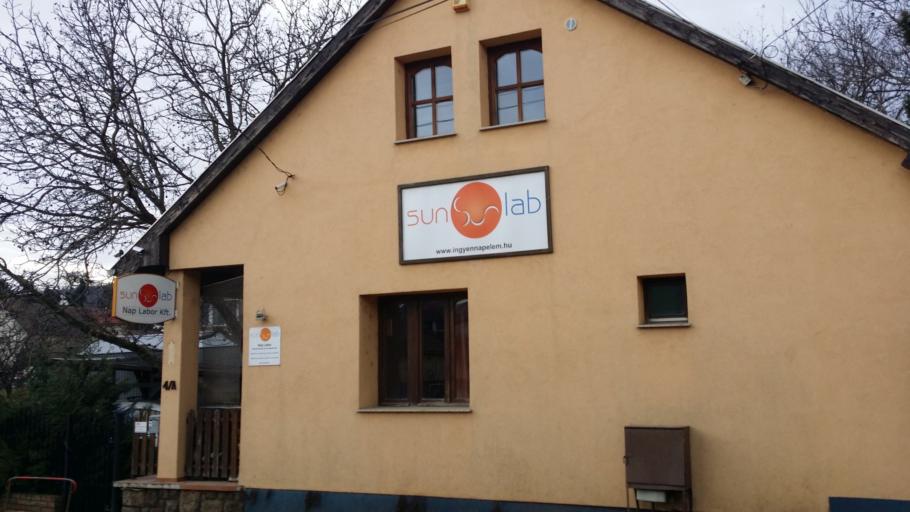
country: HU
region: Pest
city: Pilisborosjeno
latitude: 47.6058
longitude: 18.9922
